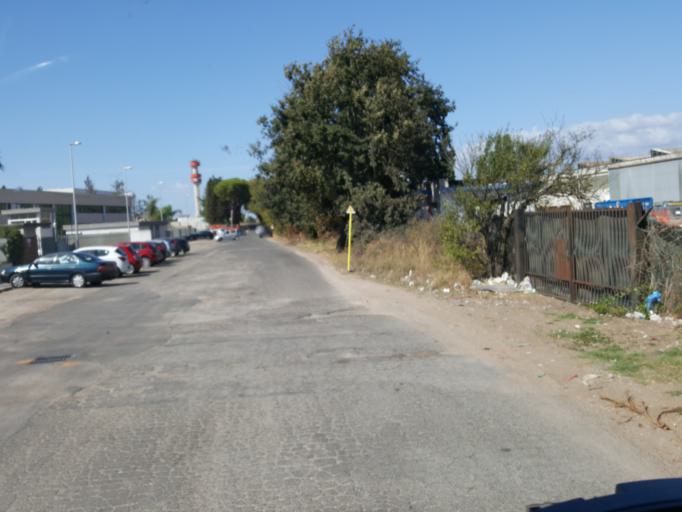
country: IT
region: Latium
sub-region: Citta metropolitana di Roma Capitale
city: Anzio
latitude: 41.5147
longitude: 12.6255
